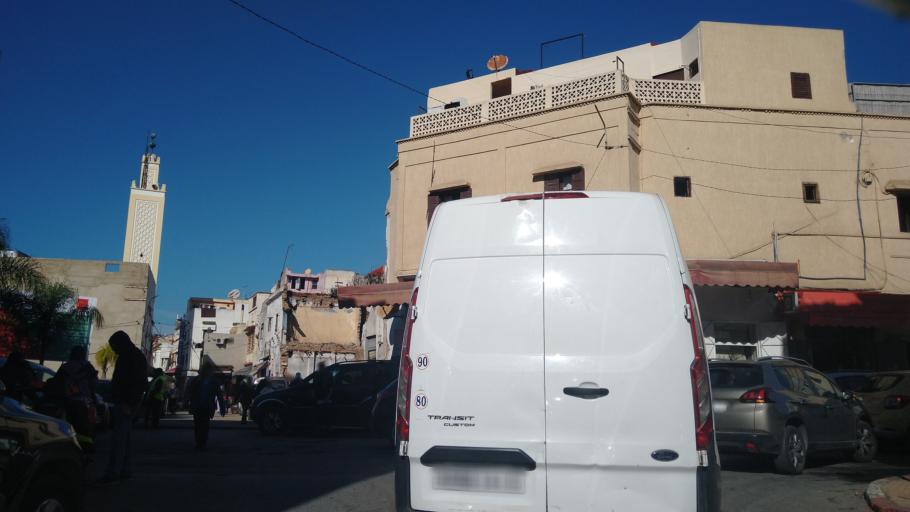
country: MA
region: Rabat-Sale-Zemmour-Zaer
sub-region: Rabat
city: Rabat
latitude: 34.0356
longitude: -6.8208
